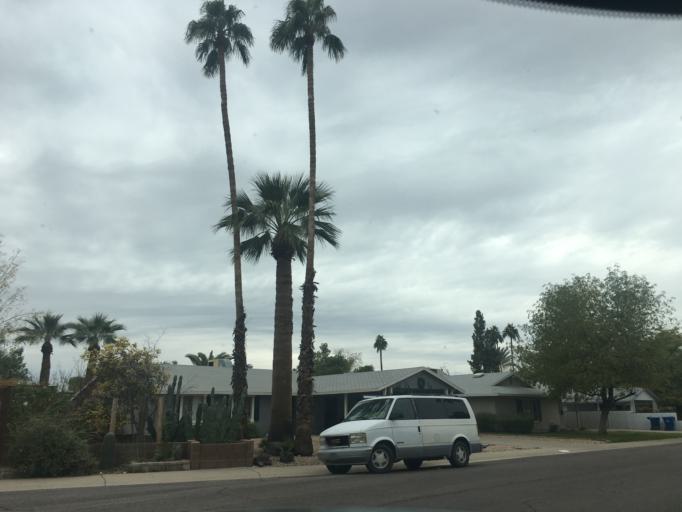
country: US
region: Arizona
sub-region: Maricopa County
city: Tempe
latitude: 33.3826
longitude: -111.9208
